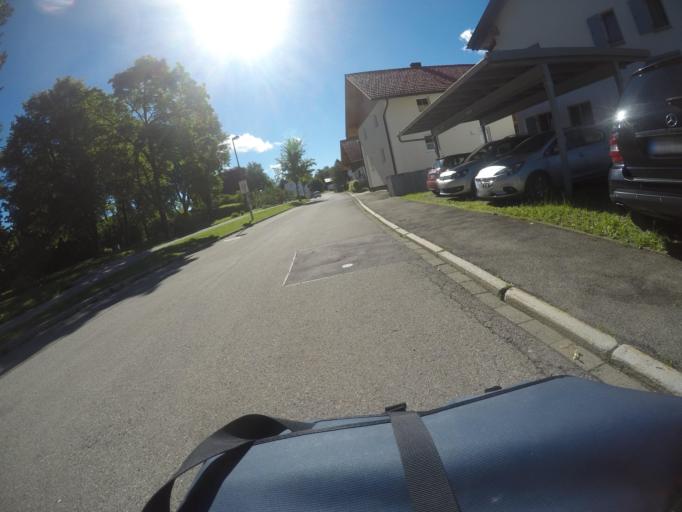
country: DE
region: Bavaria
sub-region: Swabia
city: Nesselwang
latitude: 47.6232
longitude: 10.5042
